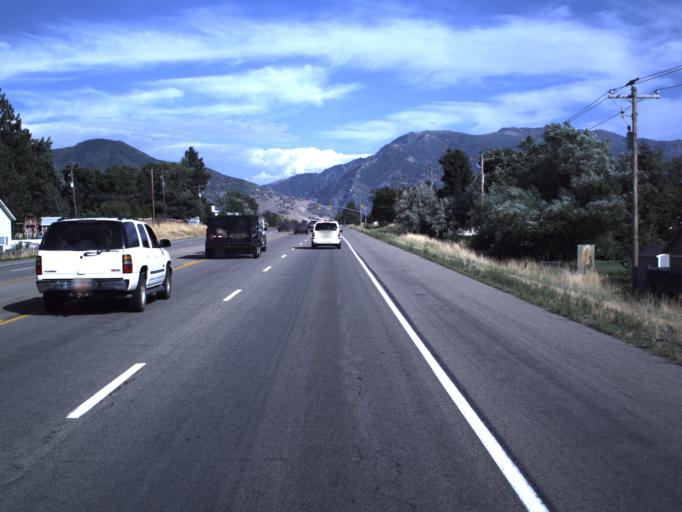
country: US
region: Utah
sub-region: Weber County
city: Washington Terrace
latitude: 41.1669
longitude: -111.9609
